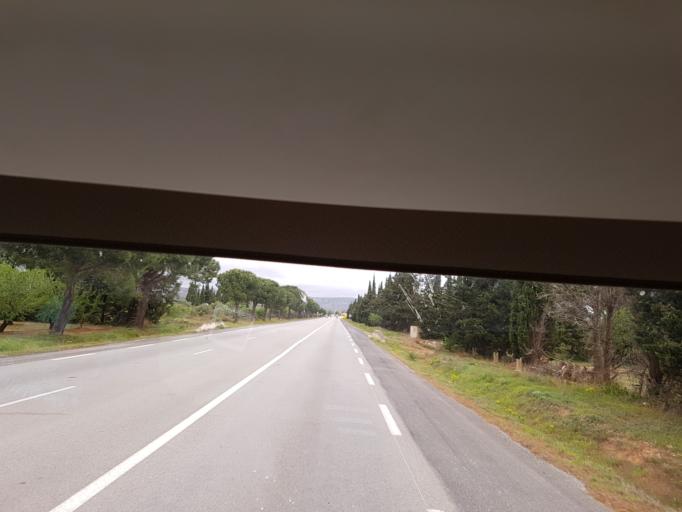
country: FR
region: Languedoc-Roussillon
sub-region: Departement des Pyrenees-Orientales
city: Salses-le-Chateau
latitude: 42.8174
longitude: 2.9153
